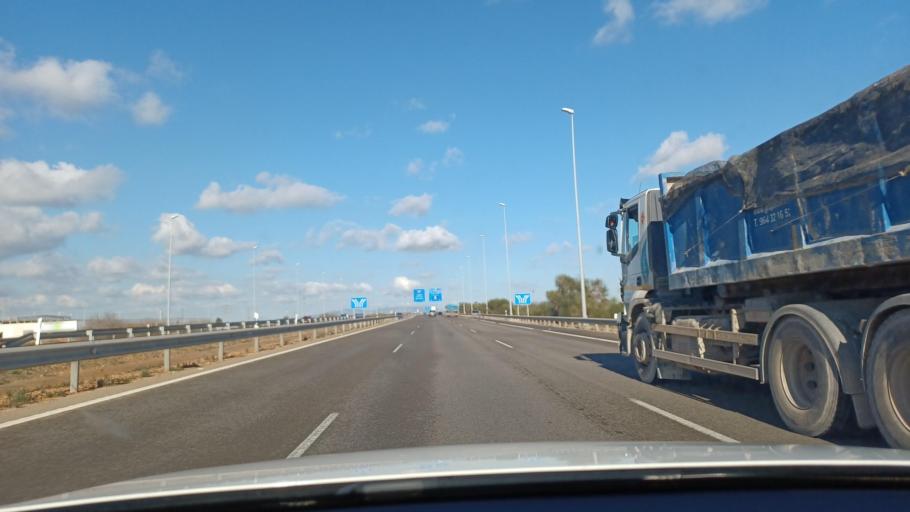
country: ES
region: Valencia
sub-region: Provincia de Castello
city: Villavieja
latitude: 39.8500
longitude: -0.1735
